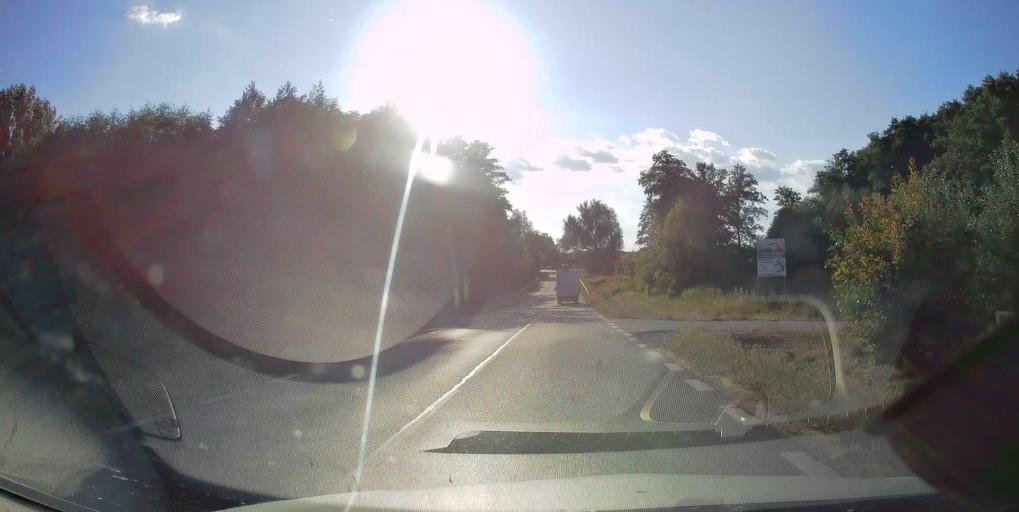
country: PL
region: Lodz Voivodeship
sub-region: Powiat rawski
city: Biala Rawska
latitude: 51.8075
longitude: 20.4972
